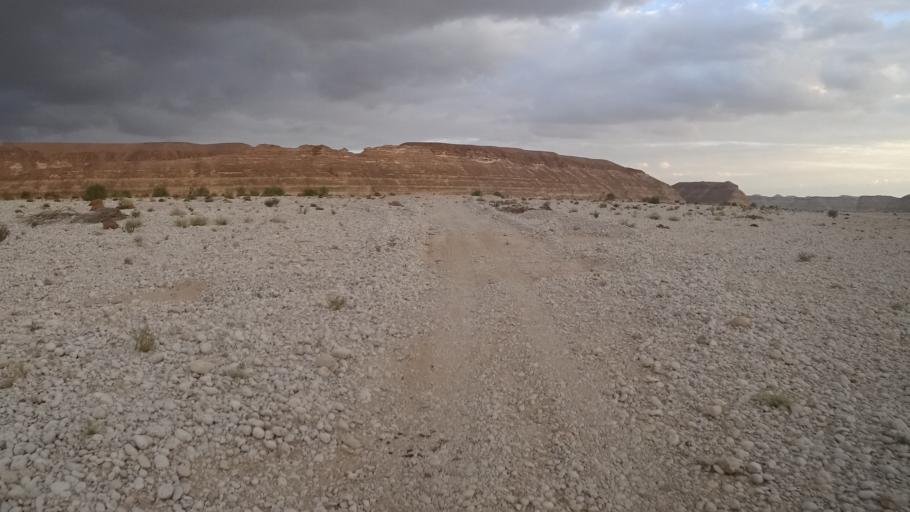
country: YE
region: Al Mahrah
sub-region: Shahan
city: Shihan as Sufla
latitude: 17.3311
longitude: 52.9196
